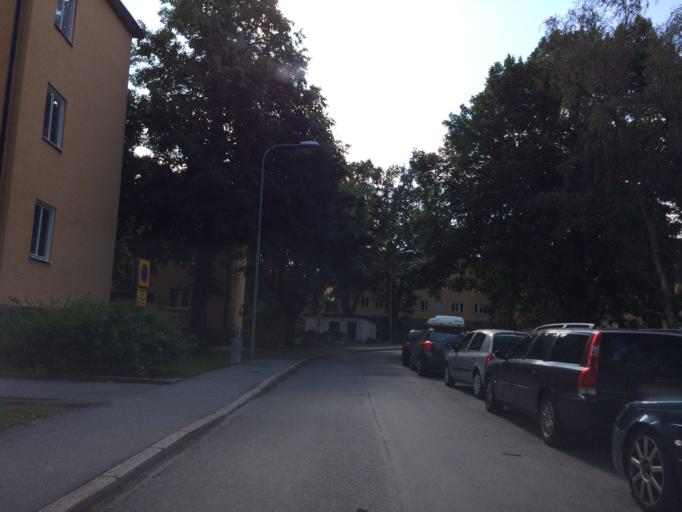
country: SE
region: Stockholm
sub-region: Stockholms Kommun
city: Arsta
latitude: 59.3021
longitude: 18.0020
